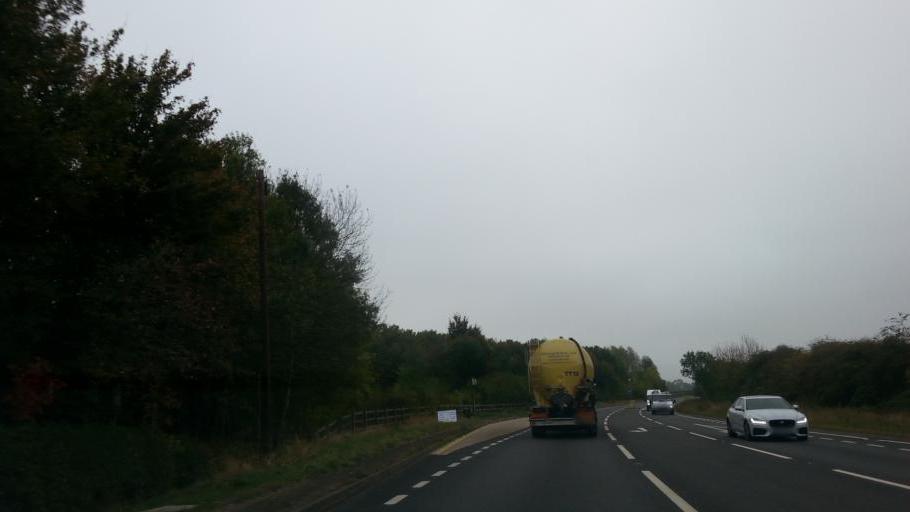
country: GB
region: England
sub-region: Northamptonshire
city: Oundle
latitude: 52.4529
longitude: -0.4621
